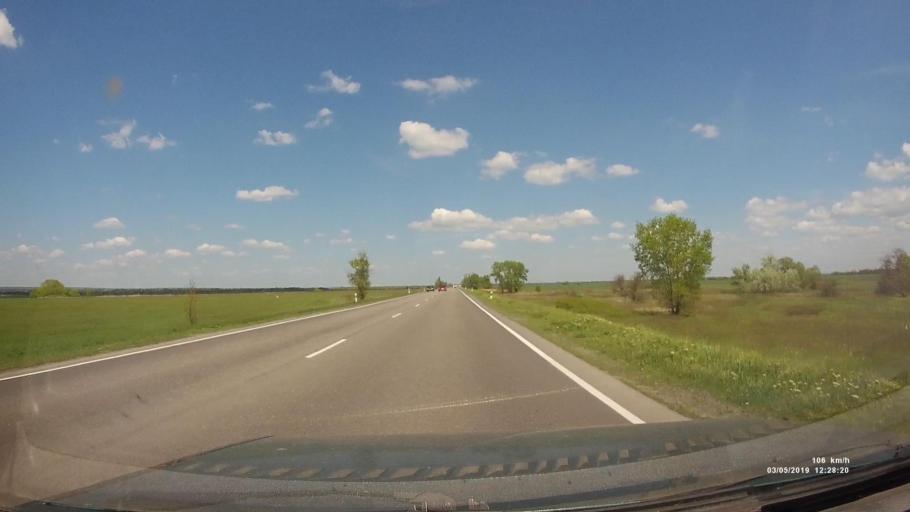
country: RU
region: Rostov
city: Semikarakorsk
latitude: 47.4715
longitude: 40.7279
